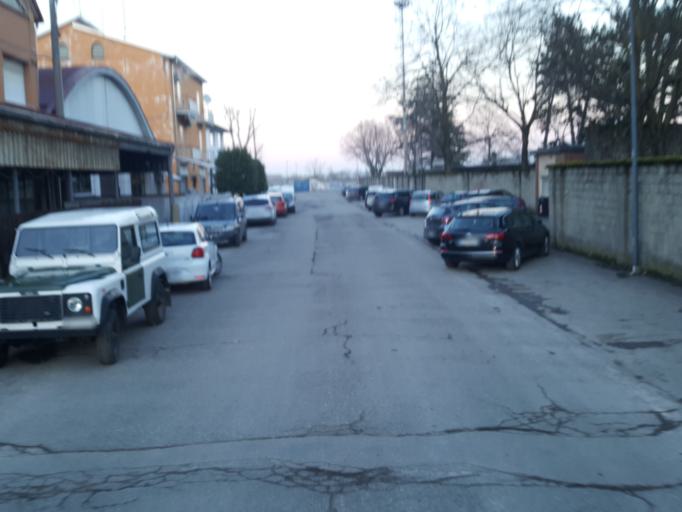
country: IT
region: Emilia-Romagna
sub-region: Provincia di Parma
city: Fornovo di Taro
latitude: 44.6949
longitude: 10.0992
